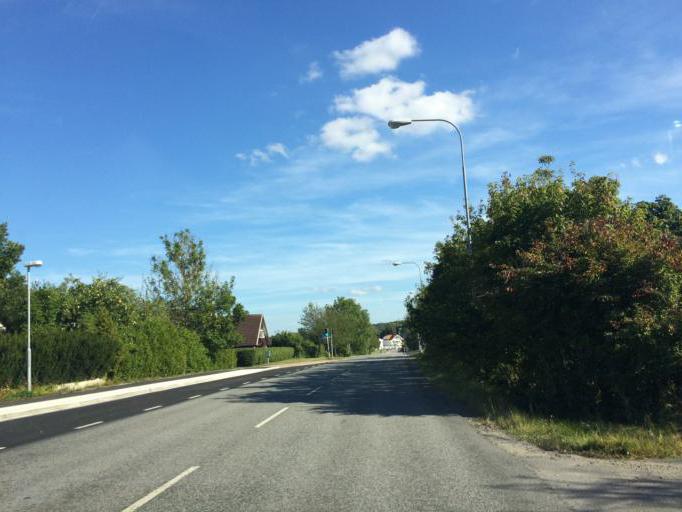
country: SE
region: Stockholm
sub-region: Upplands Vasby Kommun
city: Upplands Vaesby
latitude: 59.4942
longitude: 17.9423
